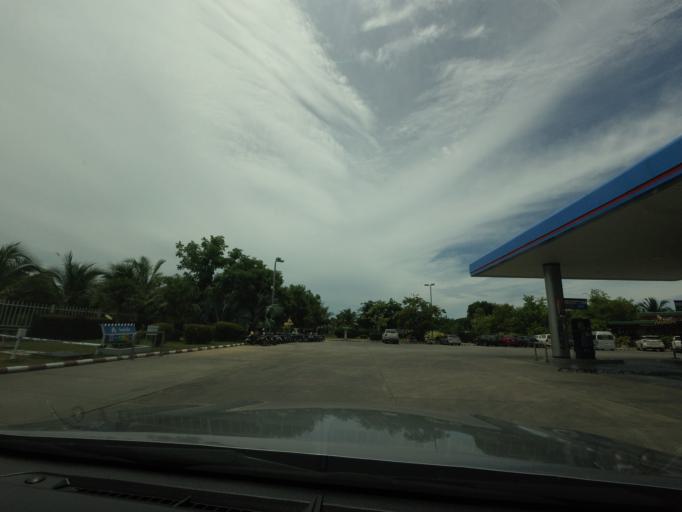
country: TH
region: Songkhla
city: Ranot
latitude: 7.7527
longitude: 100.3614
